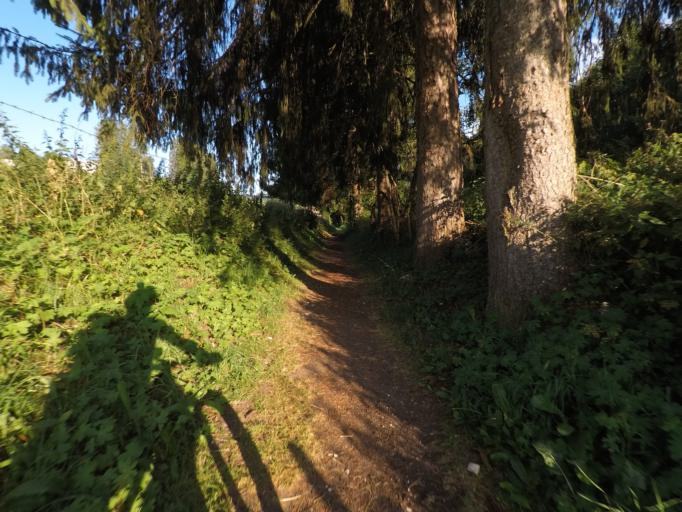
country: IT
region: Veneto
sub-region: Provincia di Vicenza
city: Asiago
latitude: 45.8666
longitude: 11.5212
